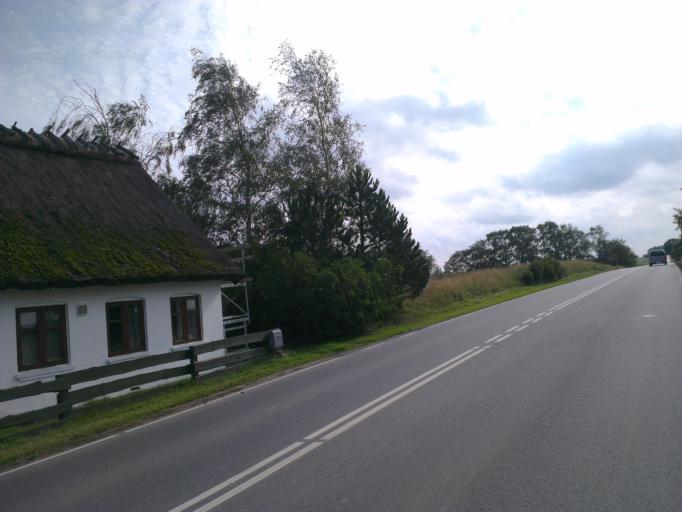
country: DK
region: Capital Region
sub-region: Frederikssund Kommune
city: Jaegerspris
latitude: 55.8892
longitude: 11.9554
